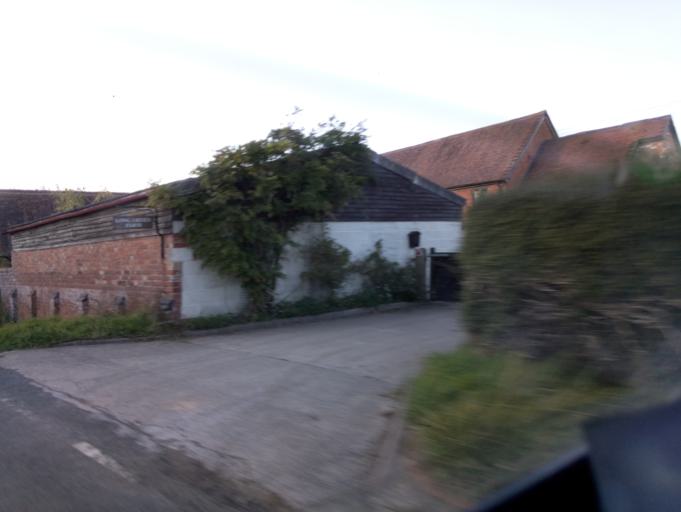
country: GB
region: England
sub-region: Worcestershire
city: Upton upon Severn
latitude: 51.9984
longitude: -2.2269
